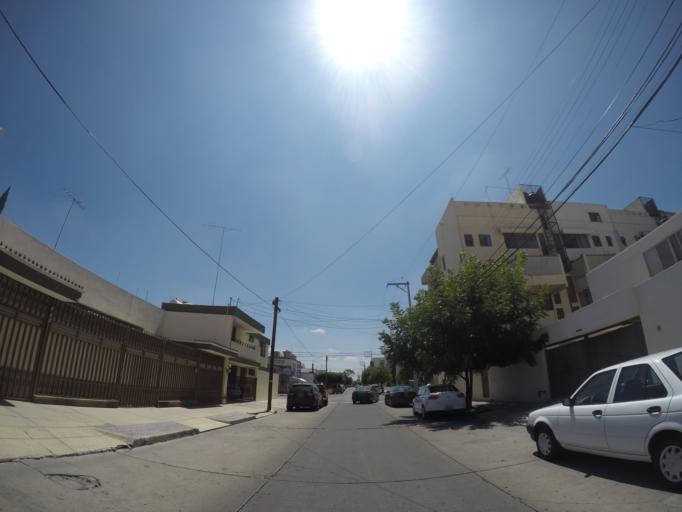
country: MX
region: San Luis Potosi
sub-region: San Luis Potosi
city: San Luis Potosi
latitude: 22.1458
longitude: -101.0037
